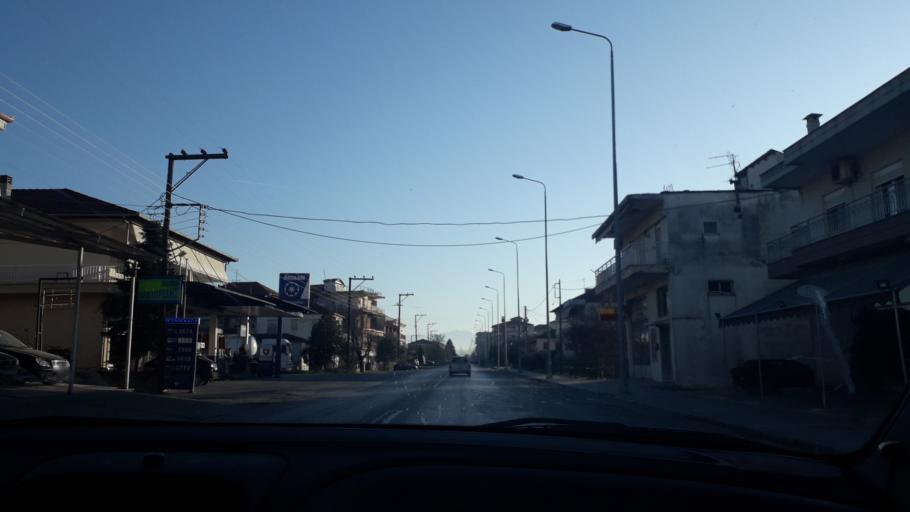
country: GR
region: Central Macedonia
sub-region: Nomos Imathias
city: Alexandreia
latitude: 40.6280
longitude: 22.4485
